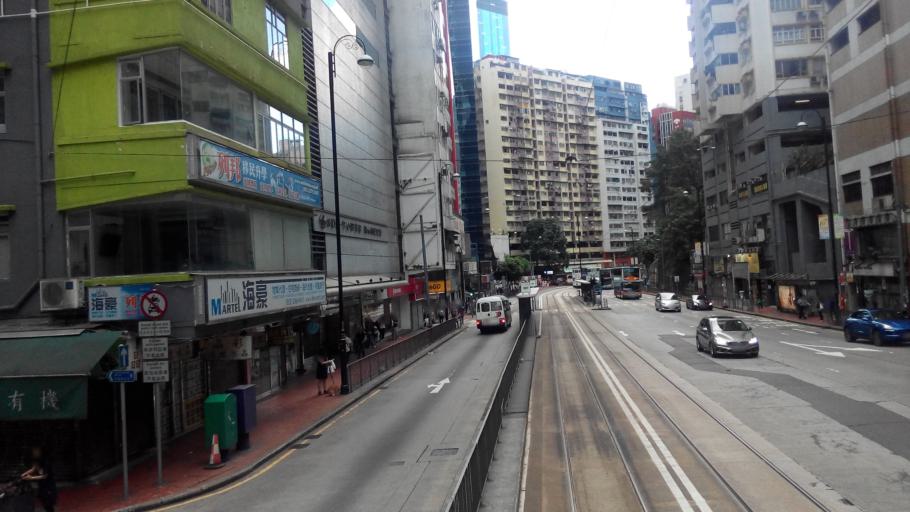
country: HK
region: Wanchai
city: Wan Chai
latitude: 22.2860
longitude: 114.1930
